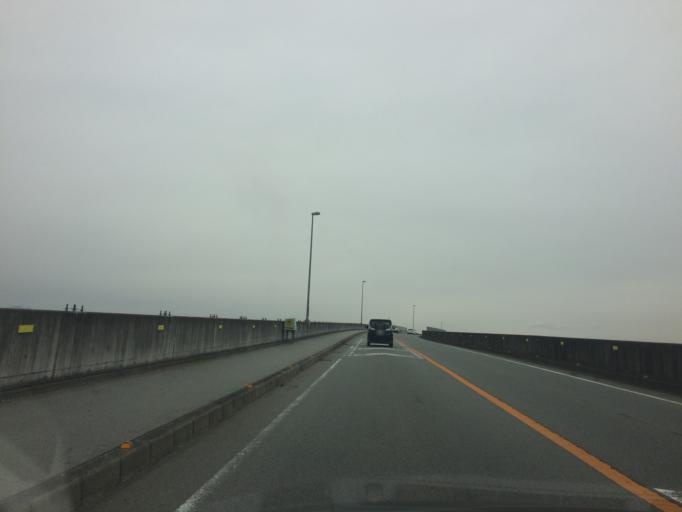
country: JP
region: Yamanashi
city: Ryuo
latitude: 35.5453
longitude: 138.4631
